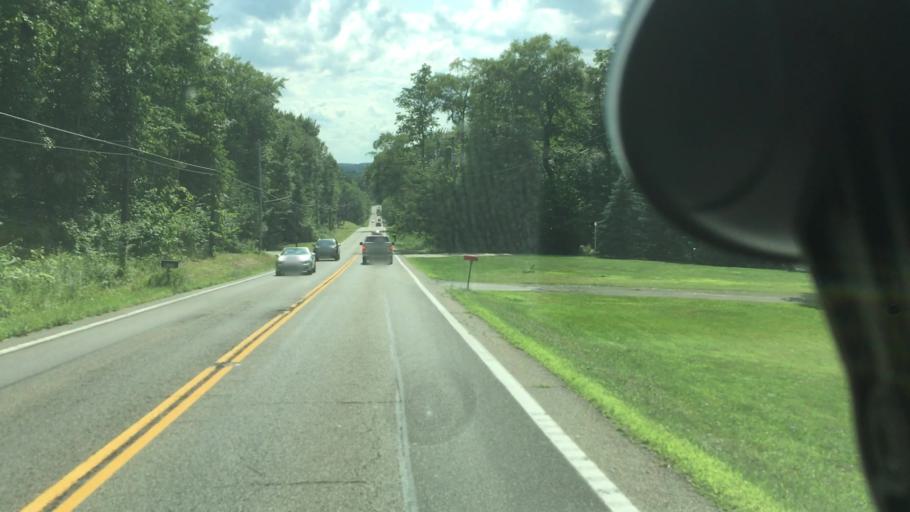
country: US
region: Ohio
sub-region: Mahoning County
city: Canfield
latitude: 40.9849
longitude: -80.8118
